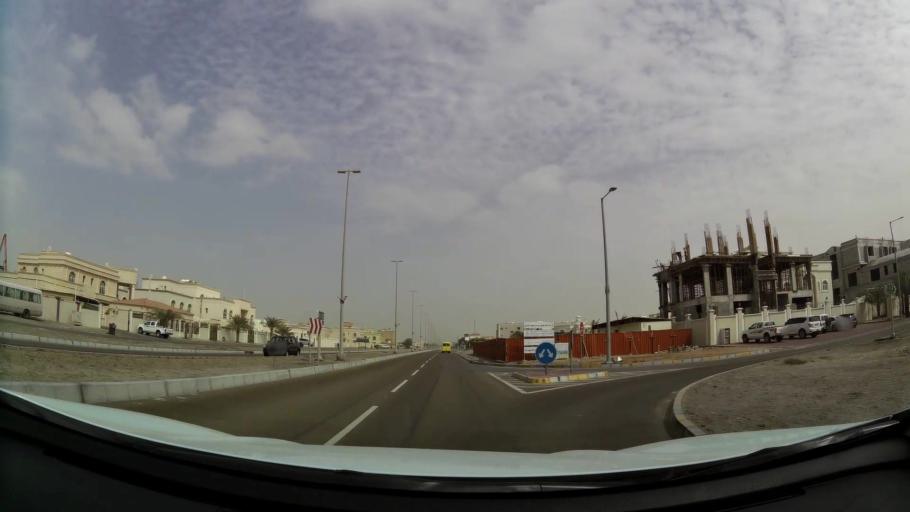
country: AE
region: Abu Dhabi
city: Abu Dhabi
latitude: 24.4092
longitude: 54.5518
